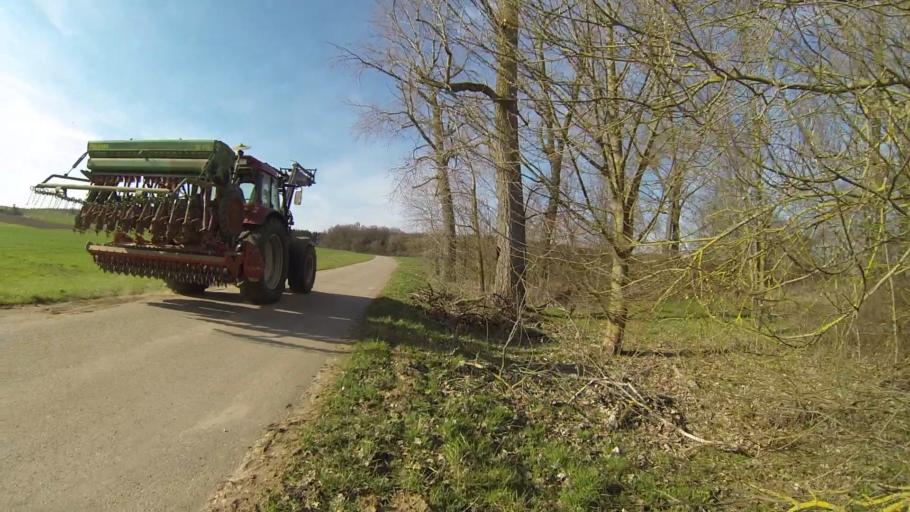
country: DE
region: Baden-Wuerttemberg
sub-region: Regierungsbezirk Stuttgart
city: Niederstotzingen
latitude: 48.5515
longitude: 10.2327
